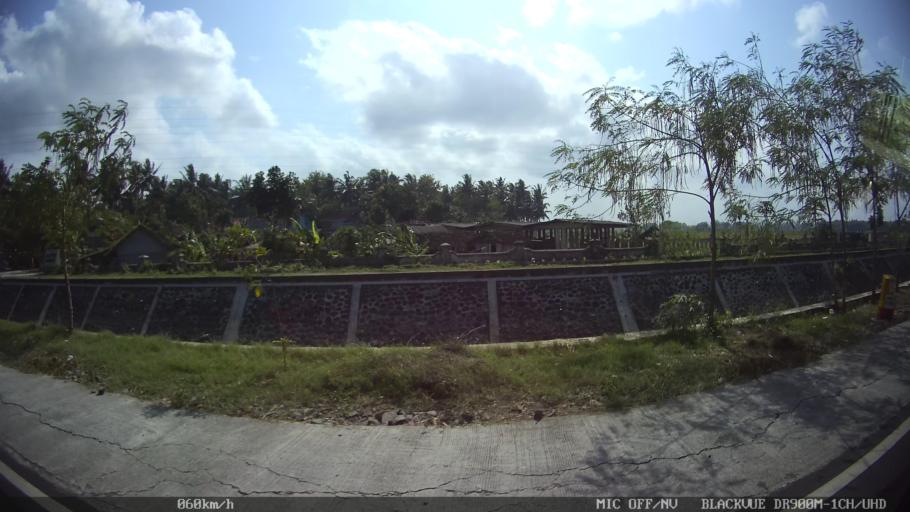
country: ID
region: Daerah Istimewa Yogyakarta
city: Srandakan
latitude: -7.9023
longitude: 110.1676
